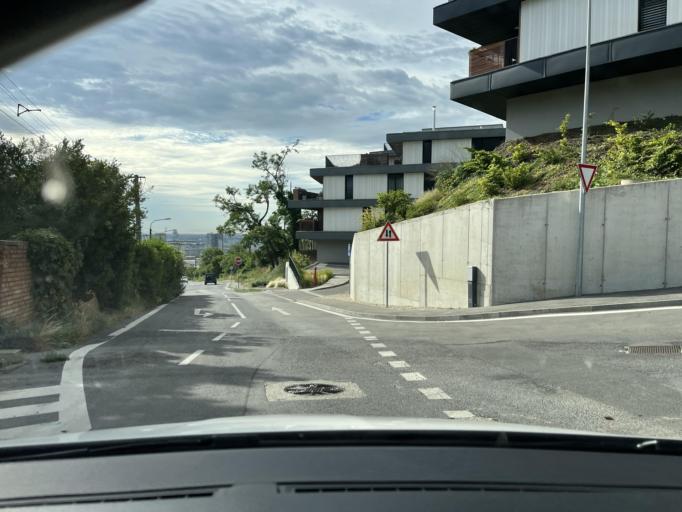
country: SK
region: Bratislavsky
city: Bratislava
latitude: 48.1658
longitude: 17.1130
